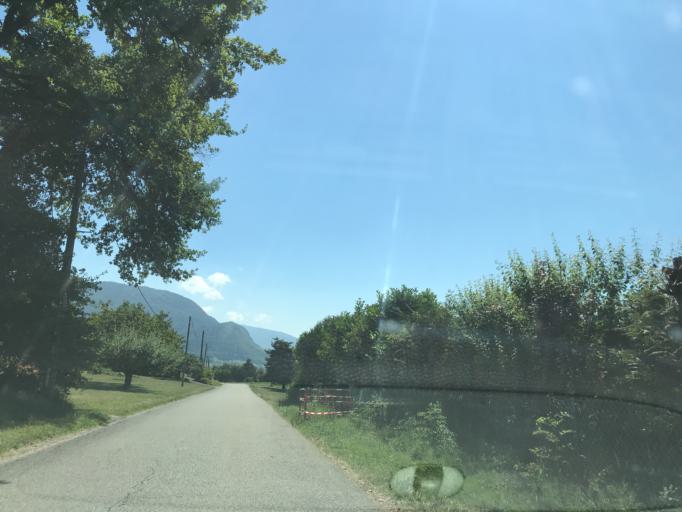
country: FR
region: Rhone-Alpes
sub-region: Departement de la Haute-Savoie
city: Villaz
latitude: 45.9489
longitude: 6.1949
